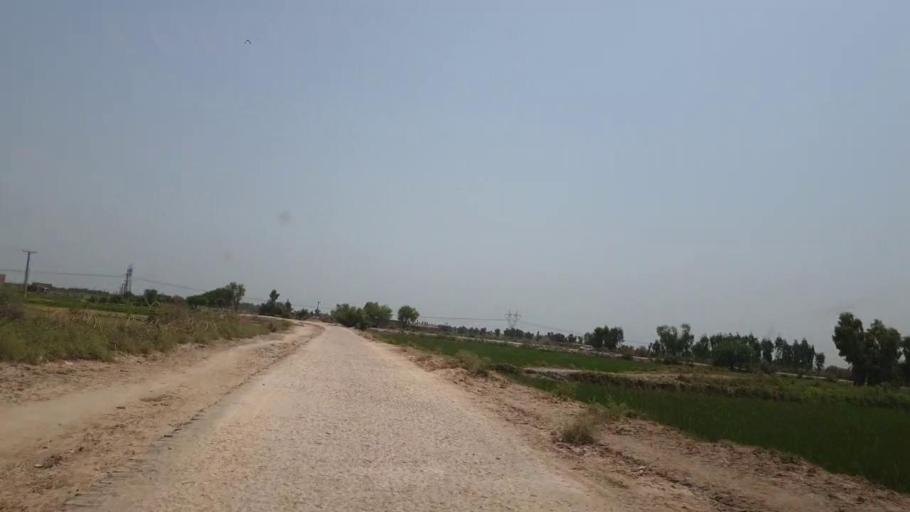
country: PK
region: Sindh
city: Garhi Yasin
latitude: 27.8496
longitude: 68.5873
